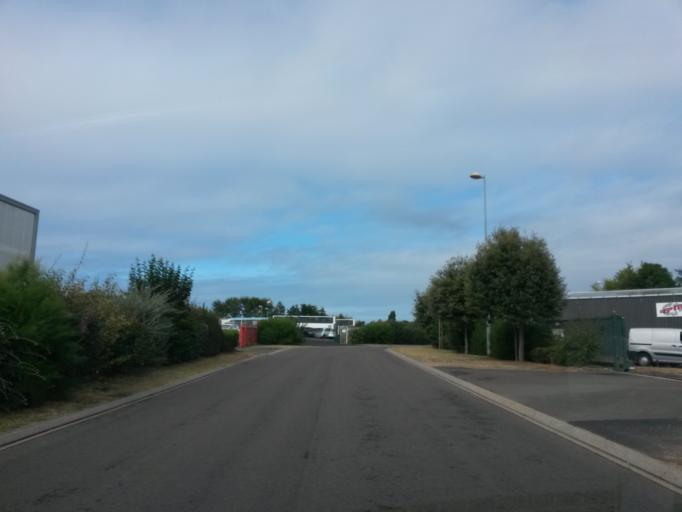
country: FR
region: Pays de la Loire
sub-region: Departement de la Vendee
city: Les Sables-d'Olonne
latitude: 46.5173
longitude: -1.7865
